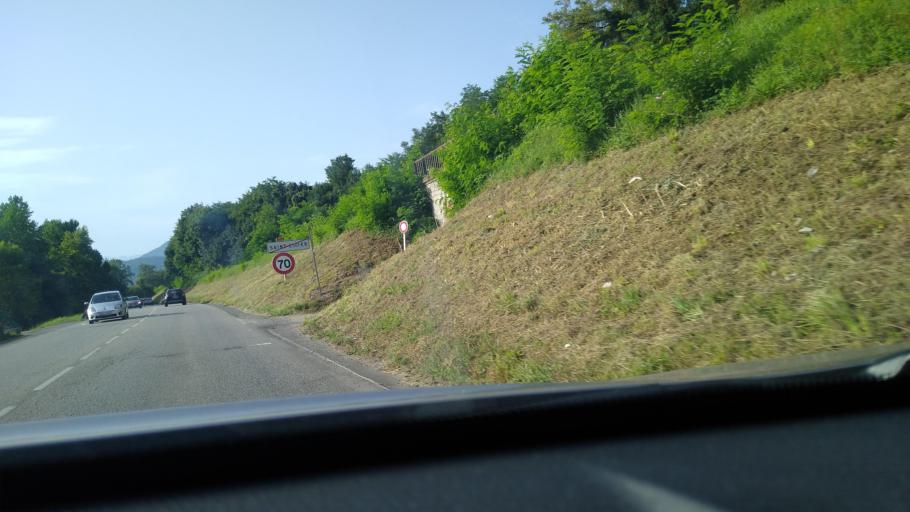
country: FR
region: Midi-Pyrenees
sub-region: Departement de l'Ariege
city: Saint-Lizier
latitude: 42.9990
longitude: 1.1350
